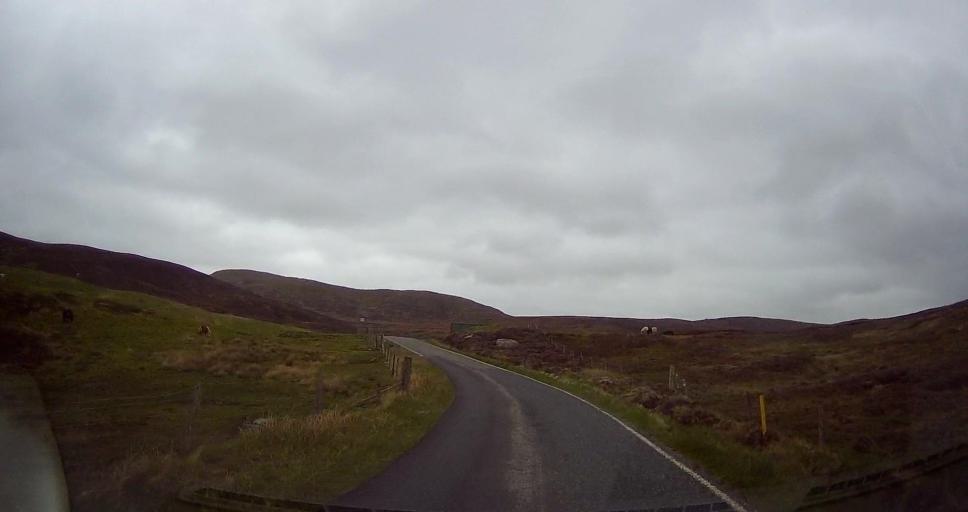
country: GB
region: Scotland
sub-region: Shetland Islands
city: Lerwick
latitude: 60.3015
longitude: -1.3451
